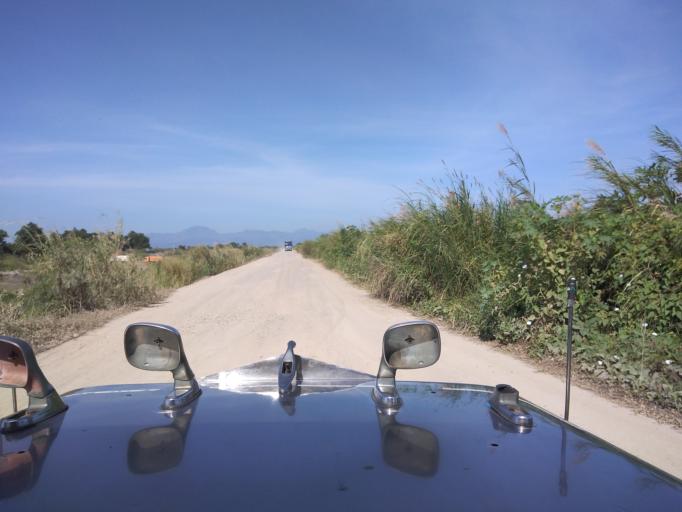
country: PH
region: Central Luzon
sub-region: Province of Pampanga
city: Bacolor
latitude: 14.9914
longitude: 120.6744
